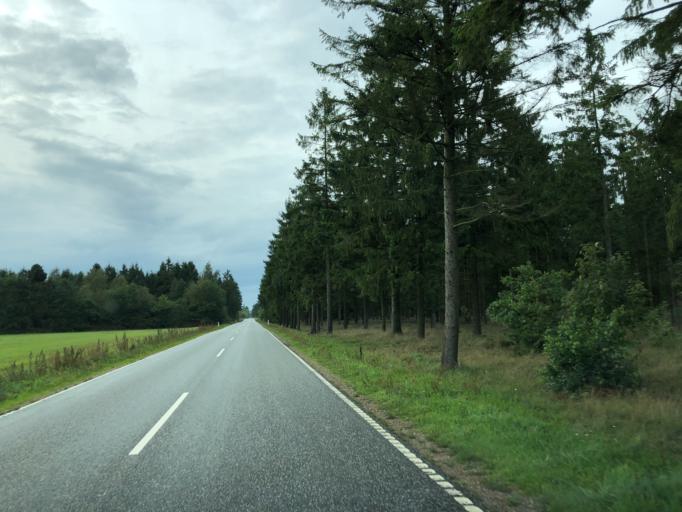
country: DK
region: Central Jutland
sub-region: Ikast-Brande Kommune
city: Brande
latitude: 55.9925
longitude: 9.2074
